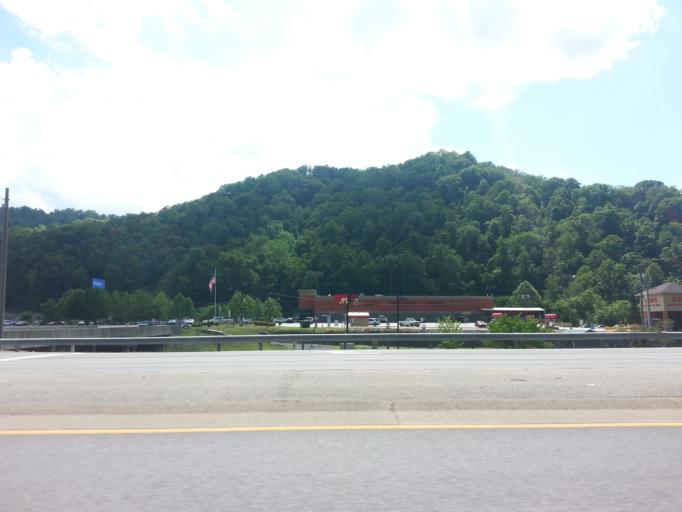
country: US
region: Kentucky
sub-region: Harlan County
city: Harlan
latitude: 36.8199
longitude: -83.3171
